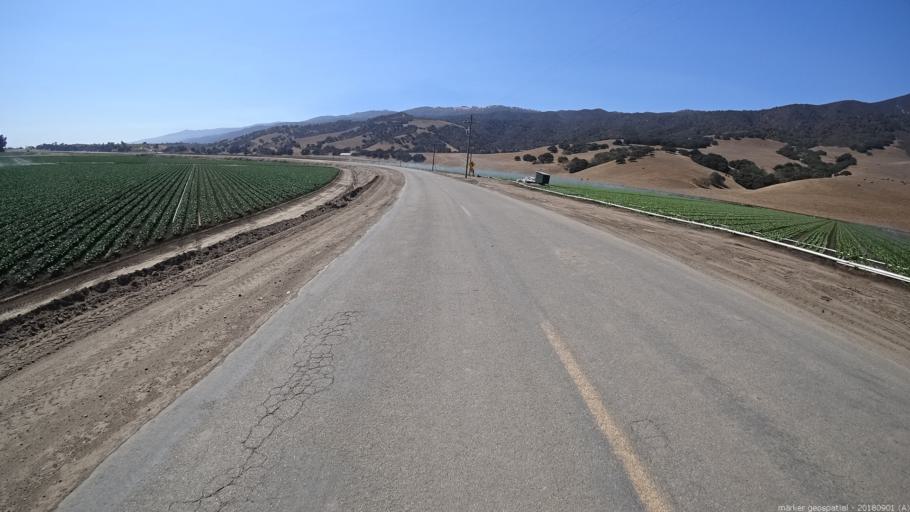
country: US
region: California
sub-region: Monterey County
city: Chualar
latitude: 36.5375
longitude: -121.5417
